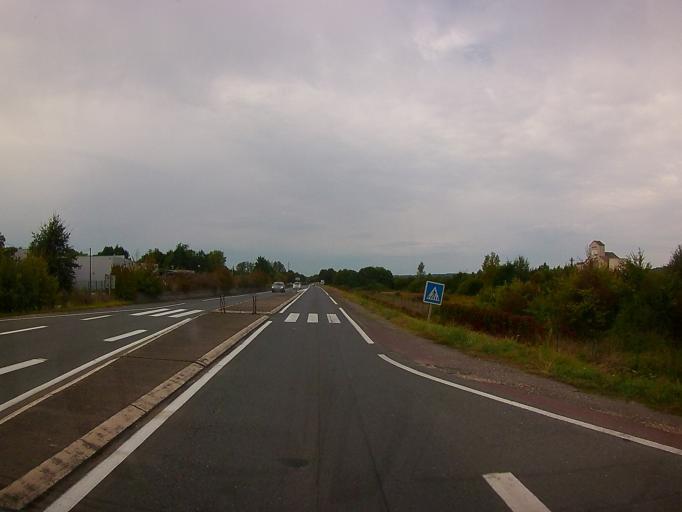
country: FR
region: Aquitaine
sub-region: Departement de la Dordogne
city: Annesse-et-Beaulieu
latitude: 45.1430
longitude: 0.5570
